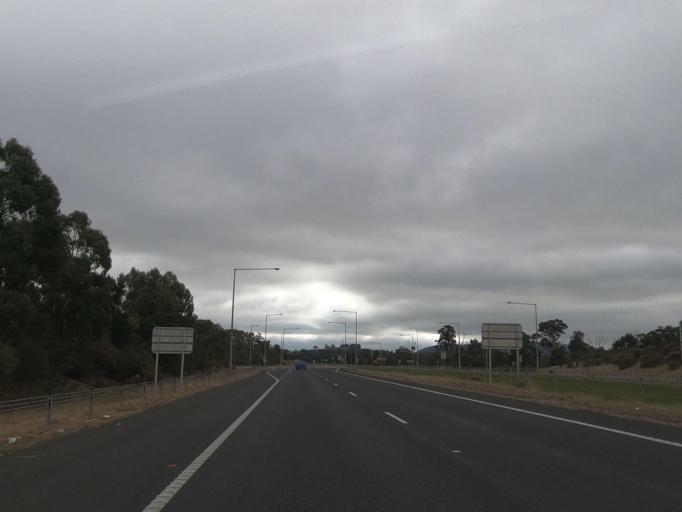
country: AU
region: Victoria
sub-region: Mount Alexander
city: Castlemaine
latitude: -37.0799
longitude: 144.3177
